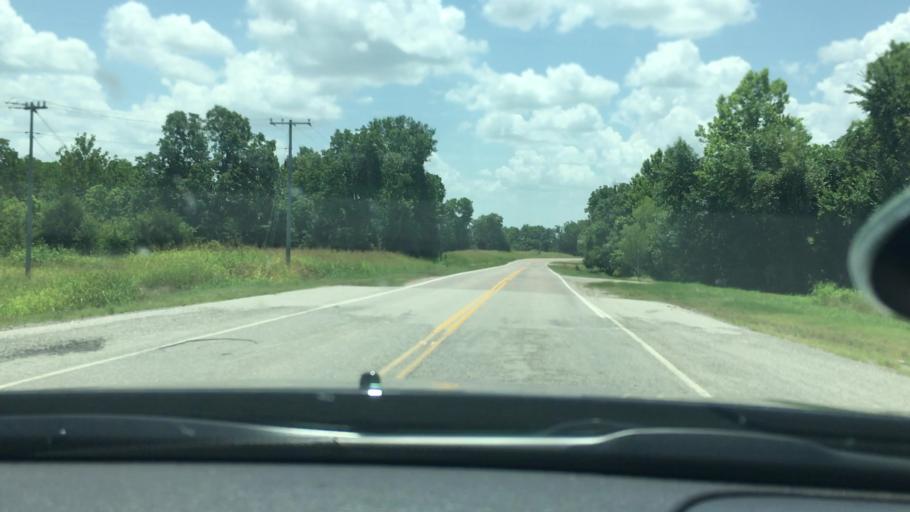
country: US
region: Oklahoma
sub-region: Johnston County
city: Tishomingo
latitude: 34.4872
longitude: -96.6269
